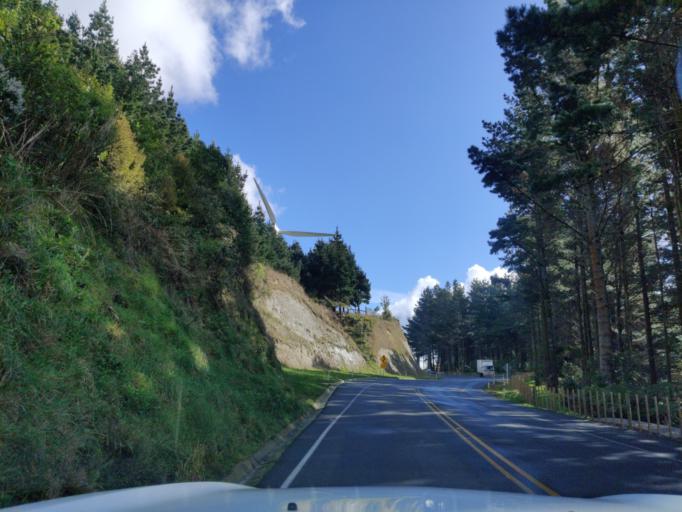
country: NZ
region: Manawatu-Wanganui
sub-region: Palmerston North City
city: Palmerston North
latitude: -40.2958
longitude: 175.8079
